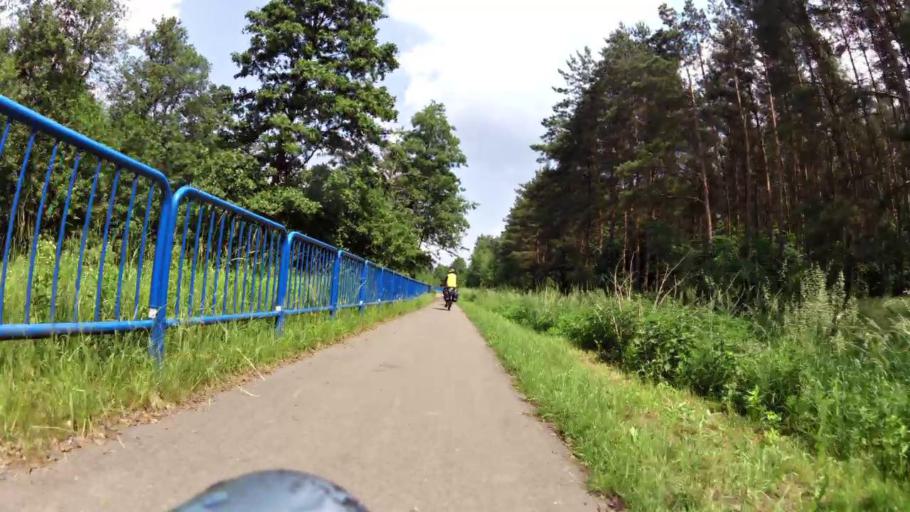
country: PL
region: Kujawsko-Pomorskie
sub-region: Powiat bydgoski
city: Koronowo
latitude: 53.2849
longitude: 17.9417
